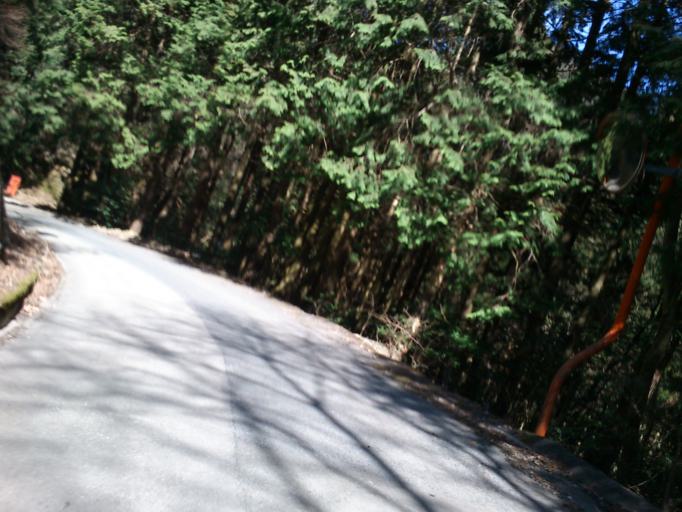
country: JP
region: Shiga Prefecture
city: Otsu-shi
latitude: 34.9524
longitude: 135.8406
